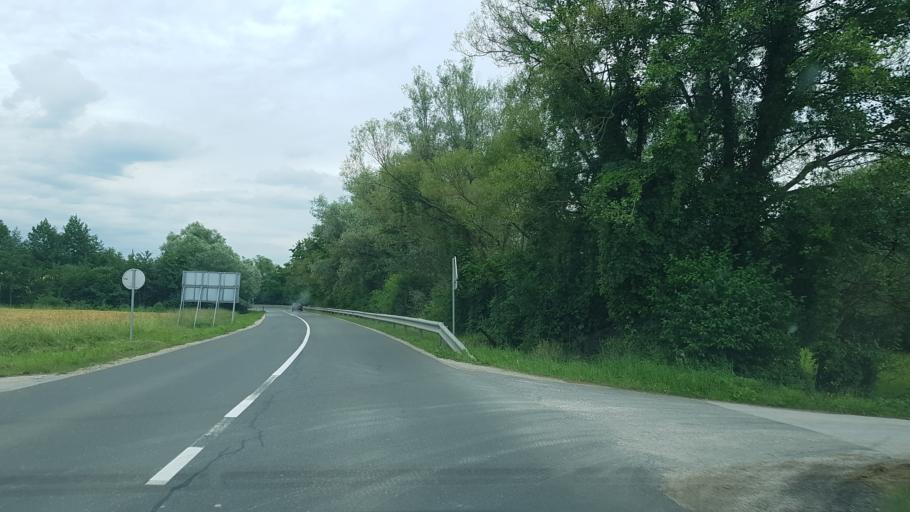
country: SI
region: Vojnik
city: Vojnik
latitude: 46.3065
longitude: 15.2865
